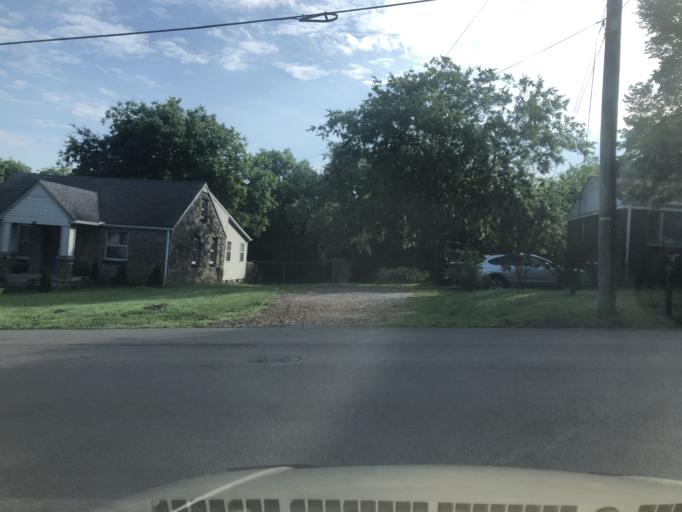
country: US
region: Tennessee
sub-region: Davidson County
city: Lakewood
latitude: 36.2473
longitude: -86.7106
